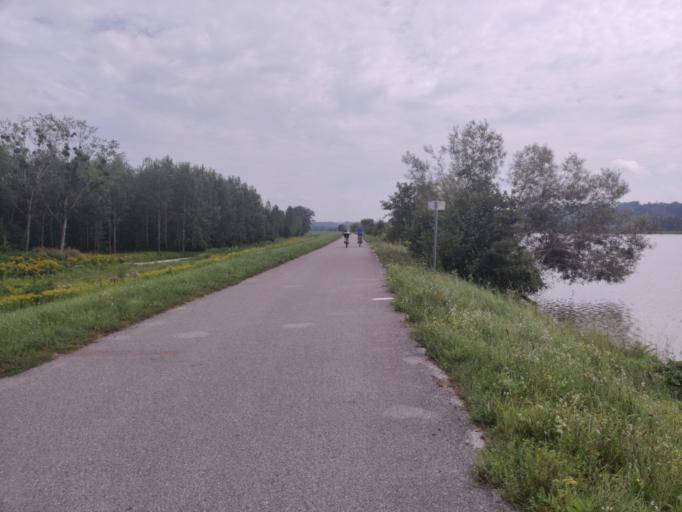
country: AT
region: Lower Austria
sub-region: Politischer Bezirk Amstetten
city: Strengberg
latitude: 48.1733
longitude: 14.6502
